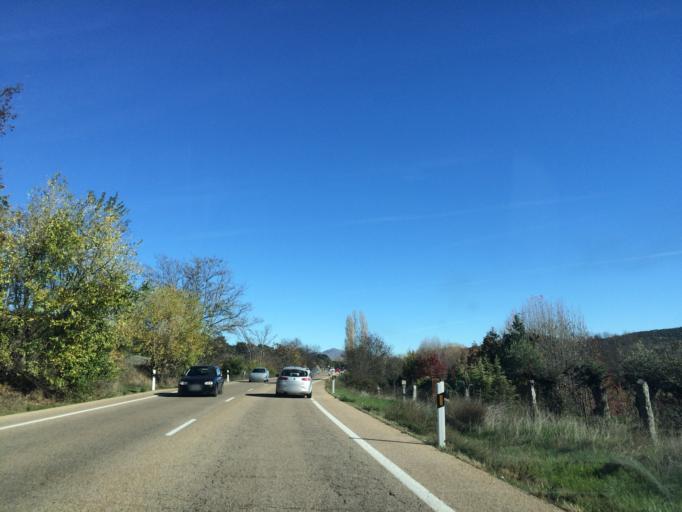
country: ES
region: Madrid
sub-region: Provincia de Madrid
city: Boalo
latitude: 40.7150
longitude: -3.8988
